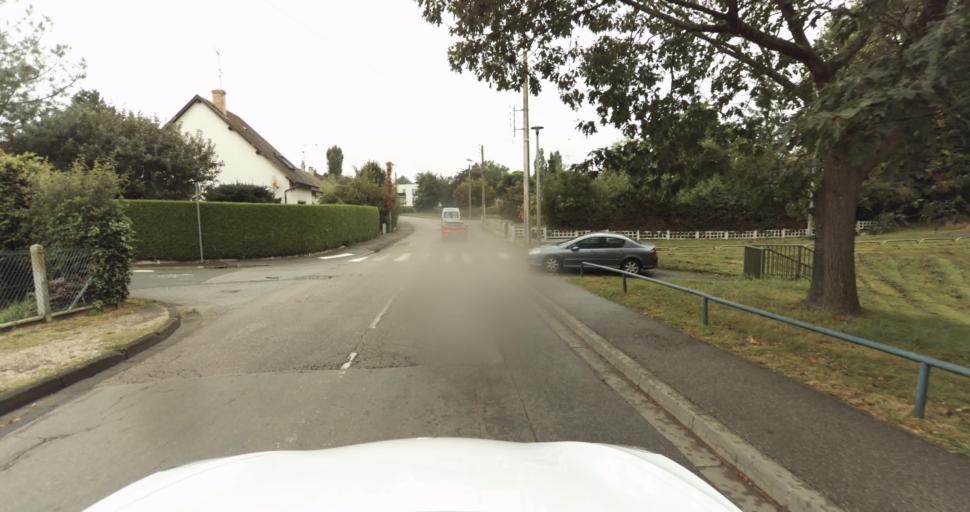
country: FR
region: Haute-Normandie
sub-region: Departement de l'Eure
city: Evreux
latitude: 49.0330
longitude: 1.1391
